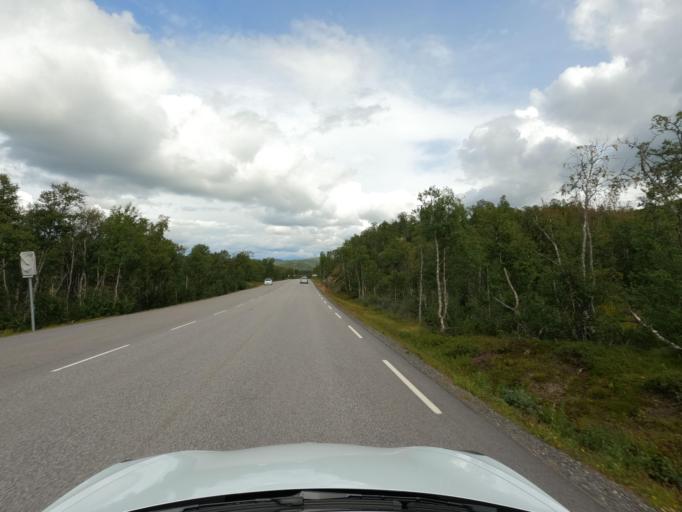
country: NO
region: Telemark
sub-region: Tinn
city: Rjukan
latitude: 59.8067
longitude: 8.2768
